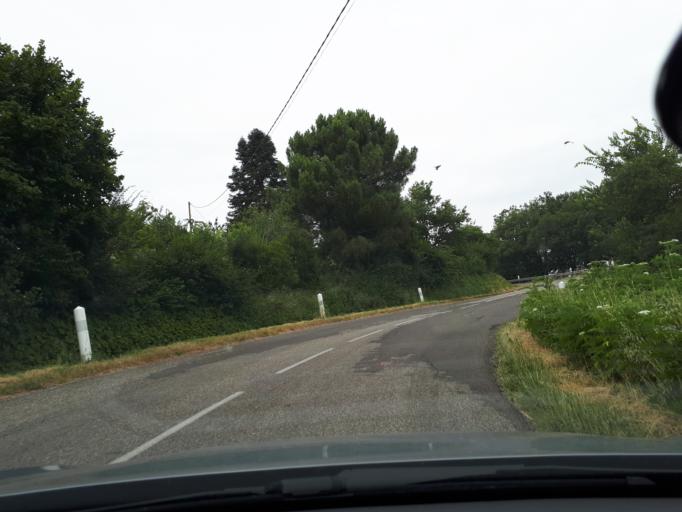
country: FR
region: Midi-Pyrenees
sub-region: Departement du Tarn-et-Garonne
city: Lamagistere
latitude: 44.0171
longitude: 0.7997
